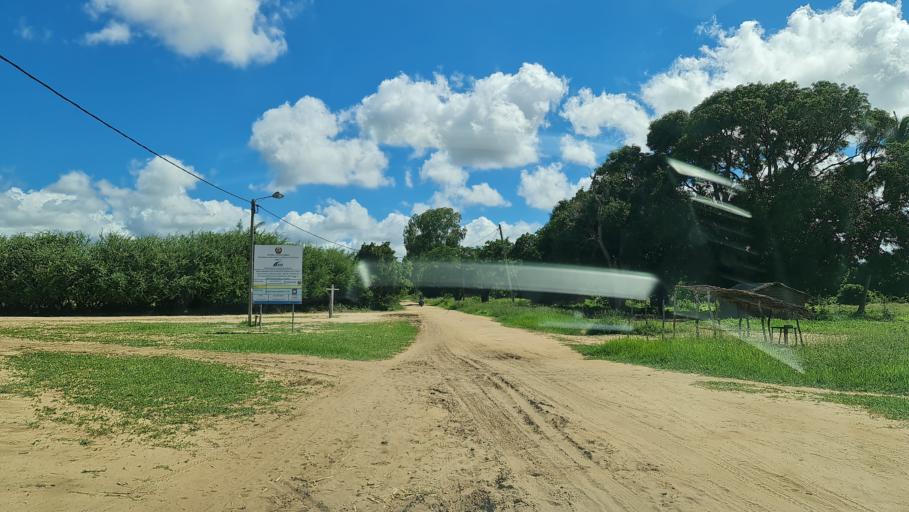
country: MZ
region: Nampula
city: Ilha de Mocambique
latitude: -15.5594
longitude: 40.4148
